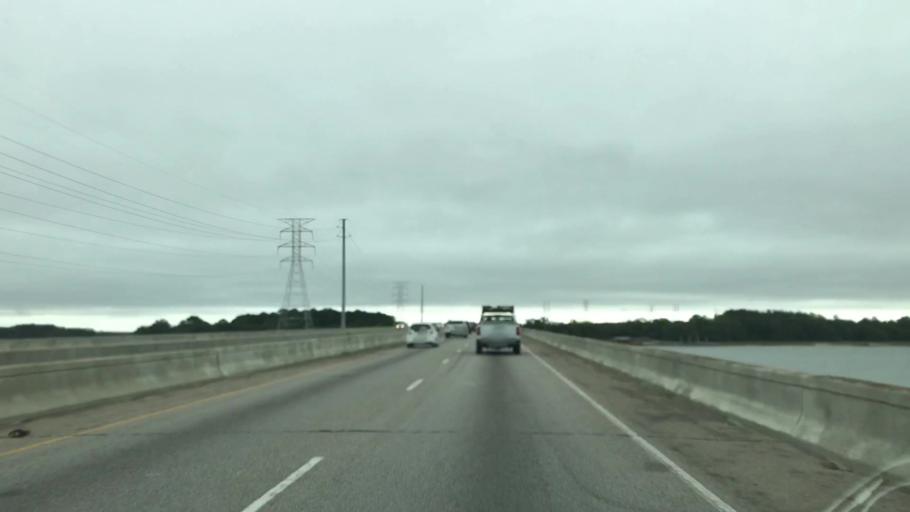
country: US
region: South Carolina
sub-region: Beaufort County
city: Hilton Head Island
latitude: 32.2313
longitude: -80.7936
